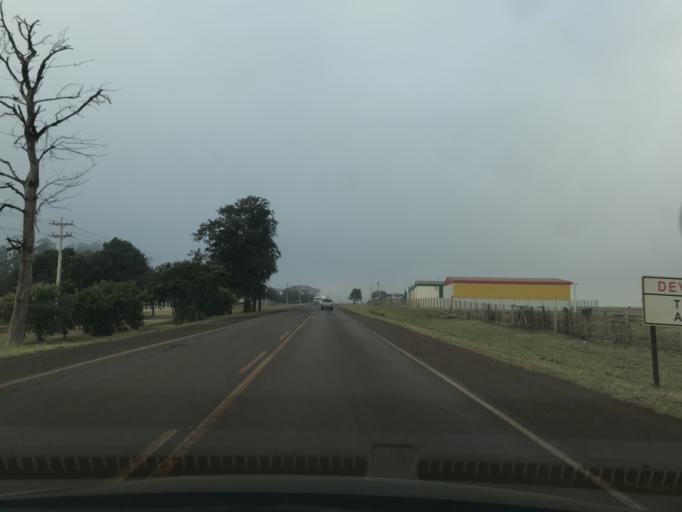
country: BR
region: Parana
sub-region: Toledo
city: Toledo
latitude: -24.6812
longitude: -53.6960
